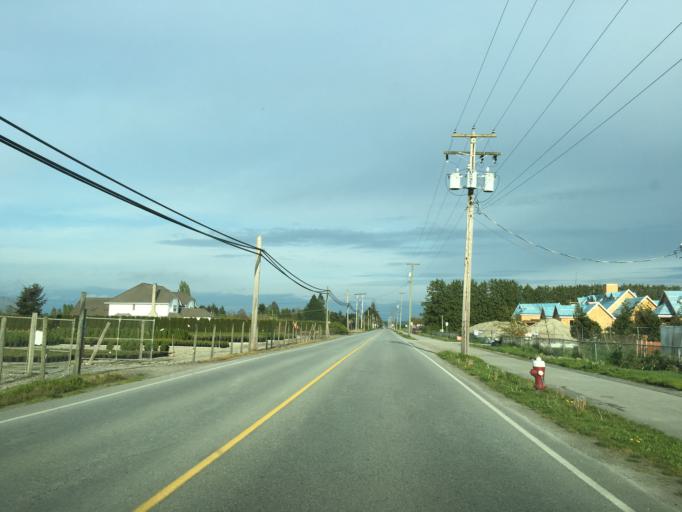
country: CA
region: British Columbia
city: Ladner
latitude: 49.1699
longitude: -123.0407
